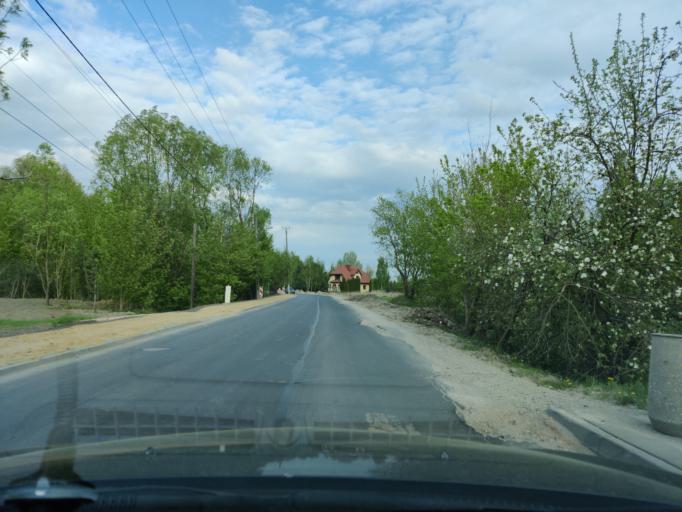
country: PL
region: Masovian Voivodeship
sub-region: Warszawa
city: Kabaty
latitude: 52.1304
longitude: 21.1159
